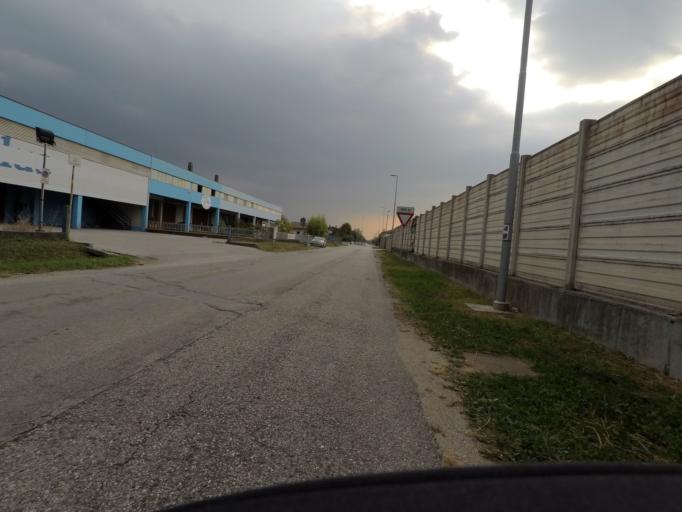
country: IT
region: Friuli Venezia Giulia
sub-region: Provincia di Udine
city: Feletto Umberto
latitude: 46.0944
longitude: 13.2423
